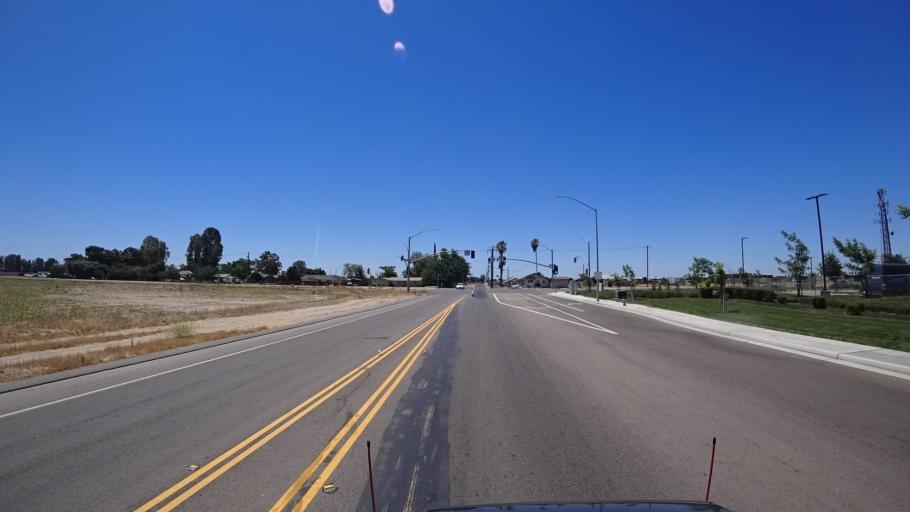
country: US
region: California
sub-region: Fresno County
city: Easton
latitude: 36.6787
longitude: -119.7637
